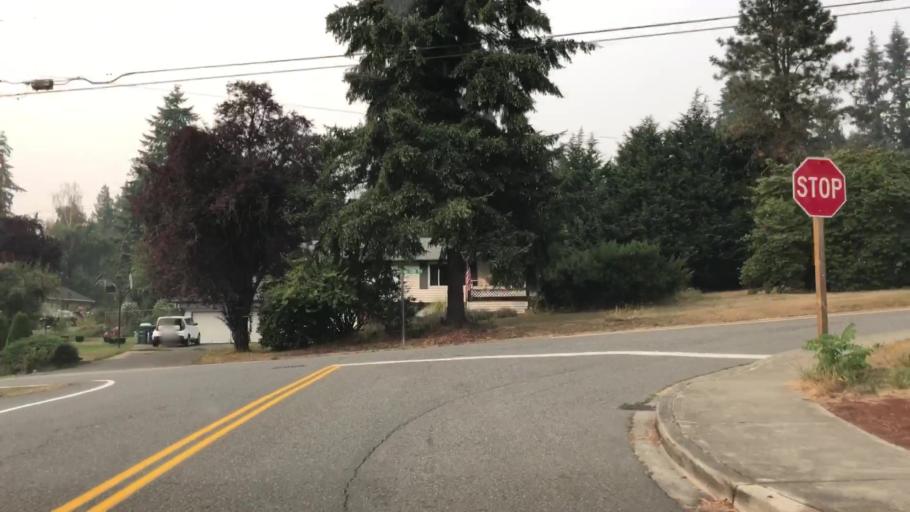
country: US
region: Washington
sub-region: King County
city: Kenmore
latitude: 47.7768
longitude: -122.2410
